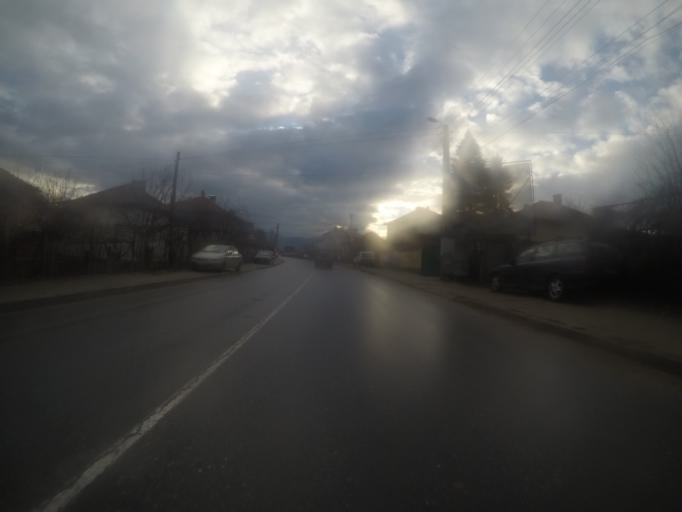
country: BG
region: Blagoevgrad
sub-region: Obshtina Simitli
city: Simitli
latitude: 41.8819
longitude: 23.1221
